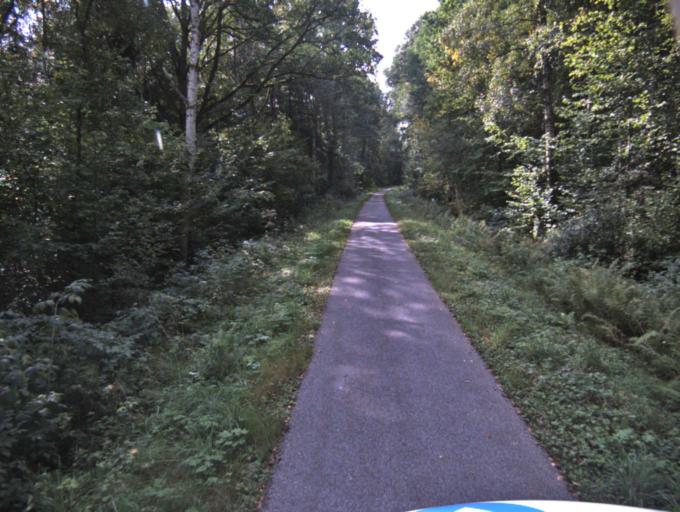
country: SE
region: Vaestra Goetaland
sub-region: Tranemo Kommun
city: Limmared
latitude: 57.6448
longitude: 13.3596
